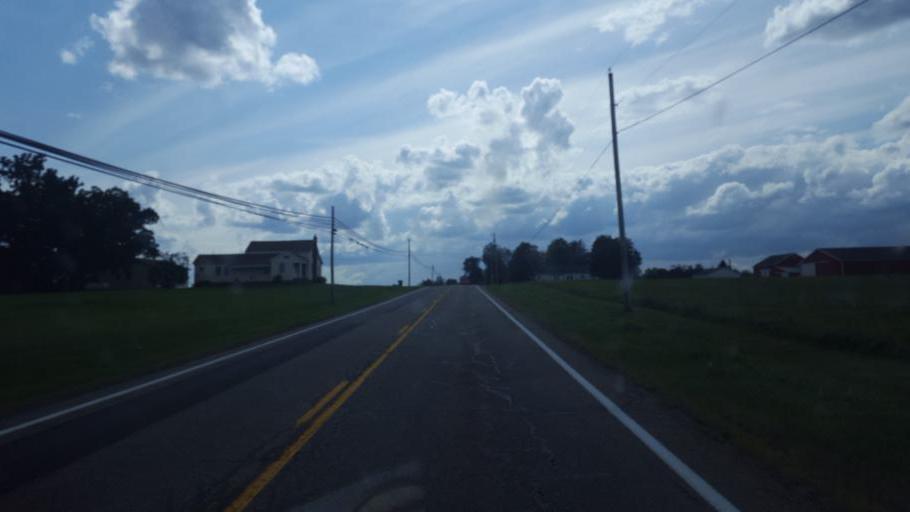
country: US
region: Ohio
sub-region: Portage County
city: Garrettsville
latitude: 41.2270
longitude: -81.1570
